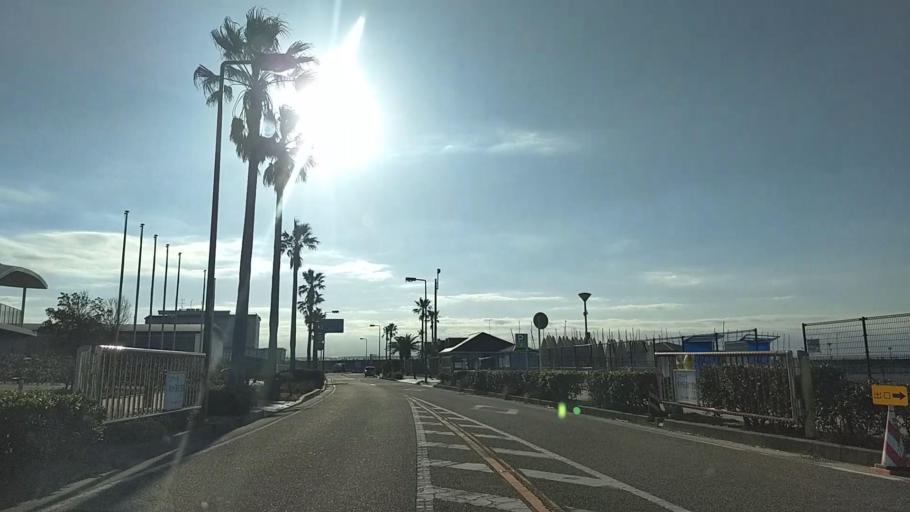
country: JP
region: Kanagawa
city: Fujisawa
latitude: 35.2997
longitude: 139.4831
